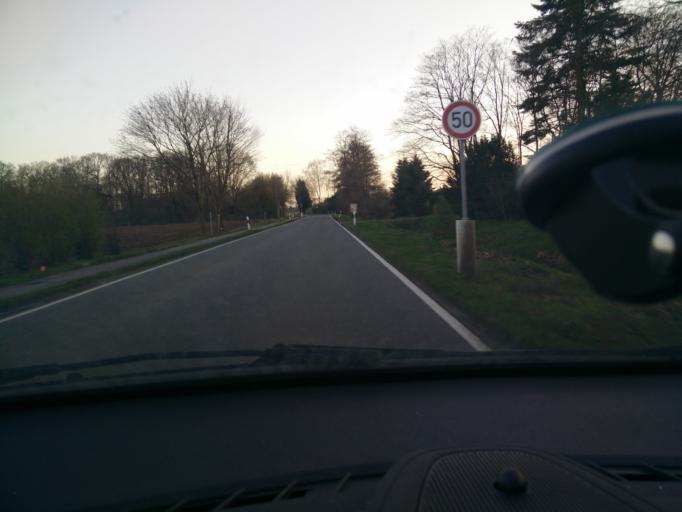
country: DE
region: North Rhine-Westphalia
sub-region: Regierungsbezirk Munster
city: Borken
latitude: 51.8049
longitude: 6.8884
